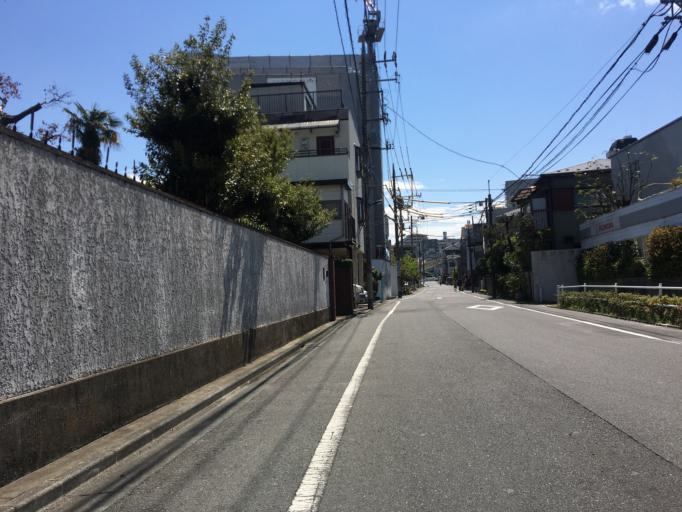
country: JP
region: Saitama
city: Kawaguchi
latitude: 35.7818
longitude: 139.6903
